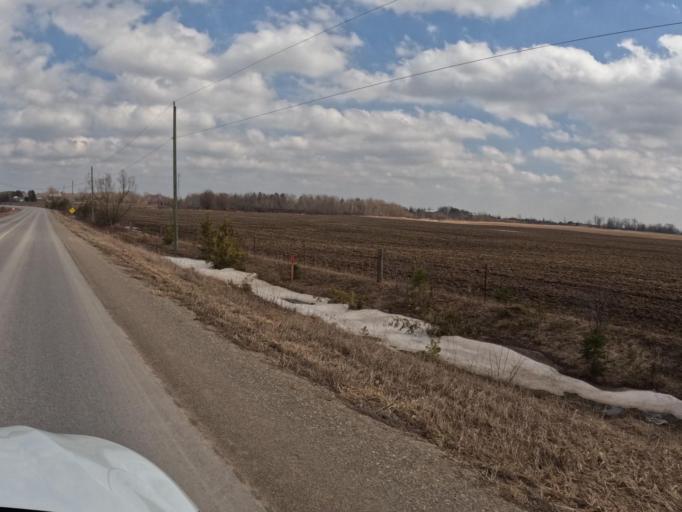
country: CA
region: Ontario
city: Shelburne
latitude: 44.0035
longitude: -80.2333
